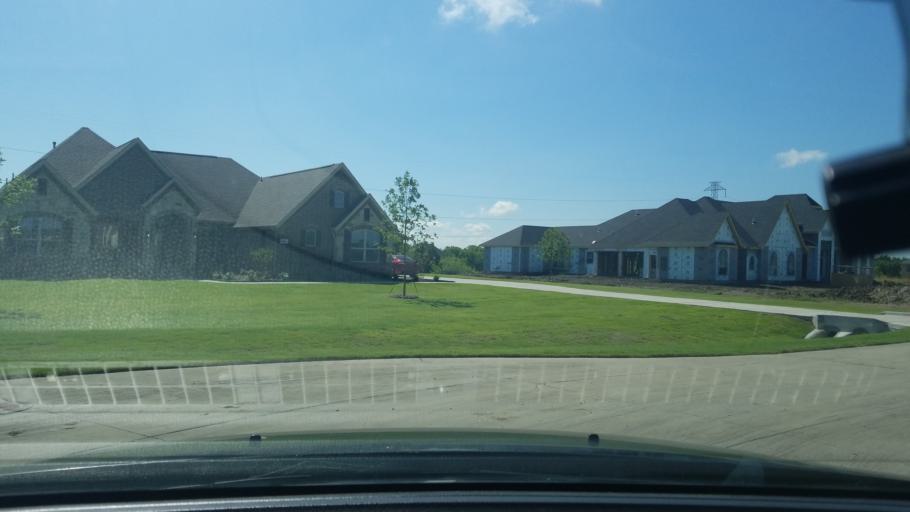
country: US
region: Texas
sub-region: Dallas County
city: Sunnyvale
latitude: 32.8015
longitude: -96.5744
